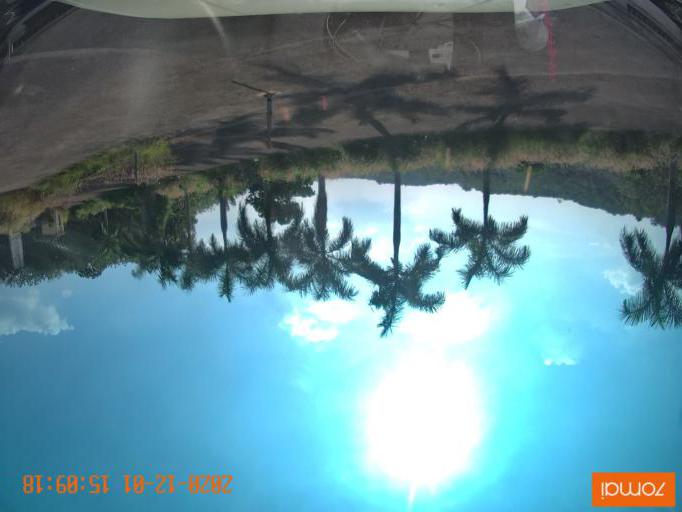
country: IN
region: Kerala
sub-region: Ernakulam
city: Ramamangalam
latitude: 9.9347
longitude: 76.5266
